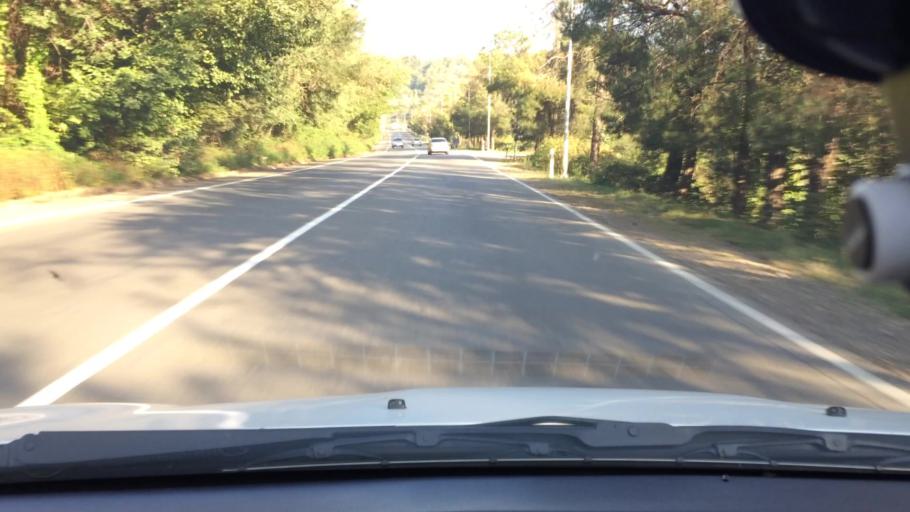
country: GE
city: Shorapani
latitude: 42.0956
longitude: 43.0764
